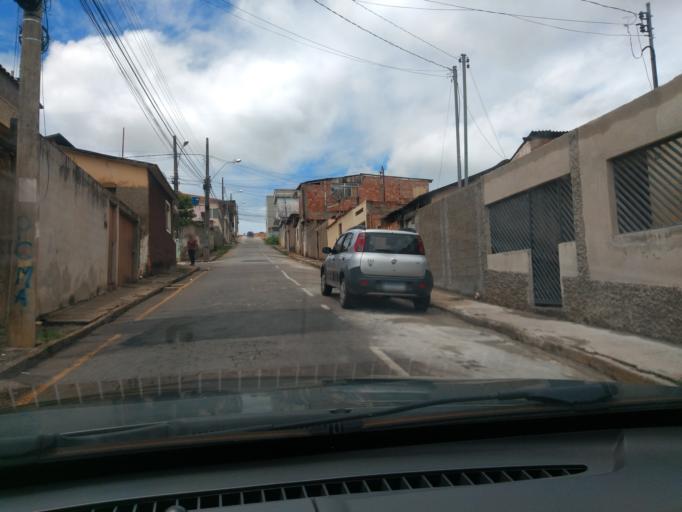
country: BR
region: Minas Gerais
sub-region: Tres Coracoes
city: Tres Coracoes
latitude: -21.6902
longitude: -45.2548
